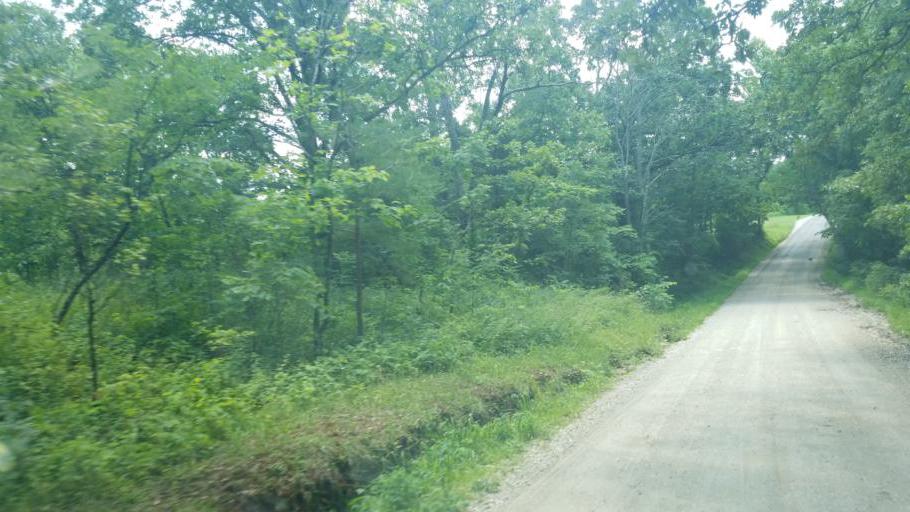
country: US
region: Ohio
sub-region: Gallia County
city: Gallipolis
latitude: 38.7248
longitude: -82.3508
